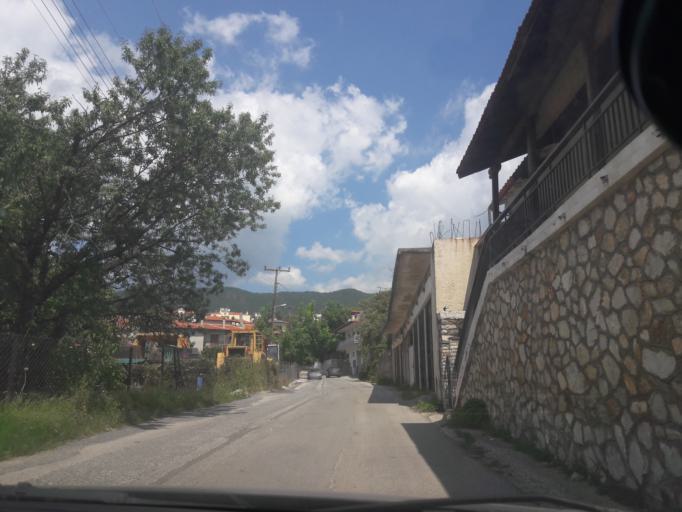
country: GR
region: Central Macedonia
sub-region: Nomos Chalkidikis
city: Polygyros
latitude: 40.3750
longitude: 23.4393
